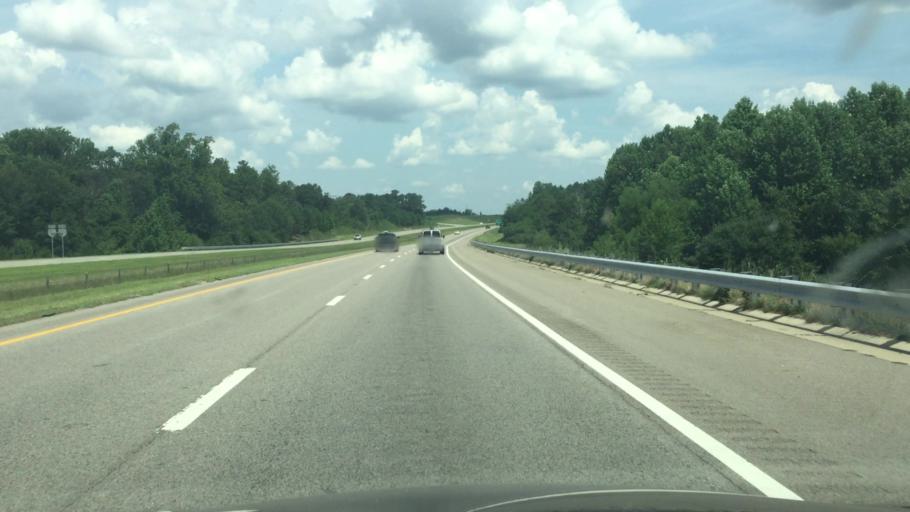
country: US
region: North Carolina
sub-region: Richmond County
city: Ellerbe
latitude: 35.1644
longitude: -79.7160
